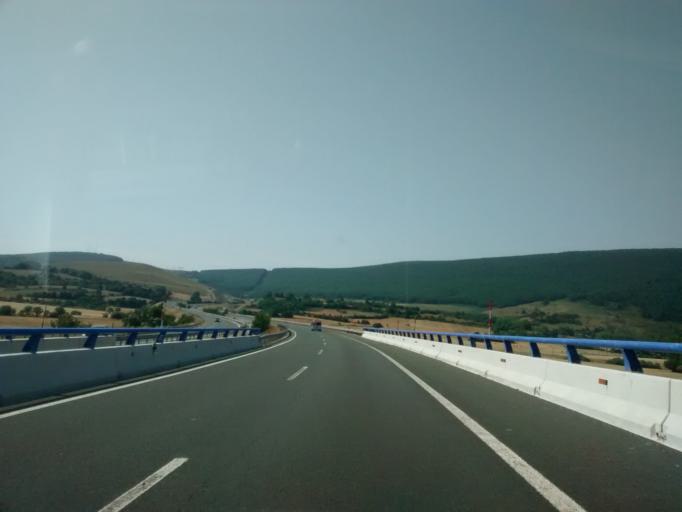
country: ES
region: Cantabria
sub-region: Provincia de Cantabria
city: Villaescusa
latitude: 42.9709
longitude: -4.1568
